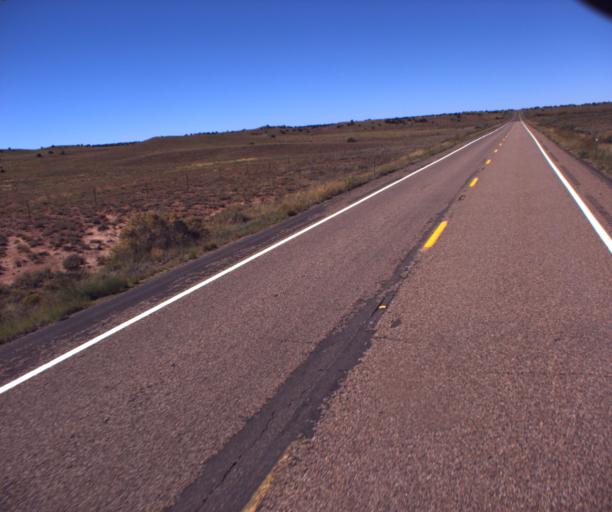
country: US
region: Arizona
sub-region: Apache County
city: Saint Johns
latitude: 34.5907
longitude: -109.6019
